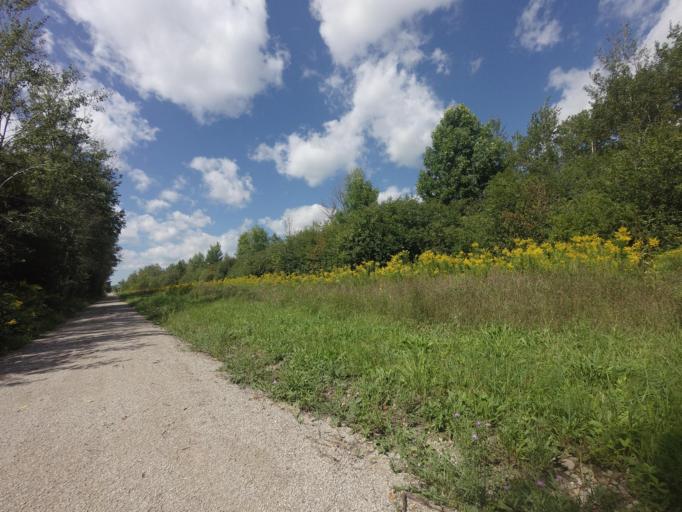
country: CA
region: Ontario
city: Huron East
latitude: 43.6342
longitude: -81.1877
